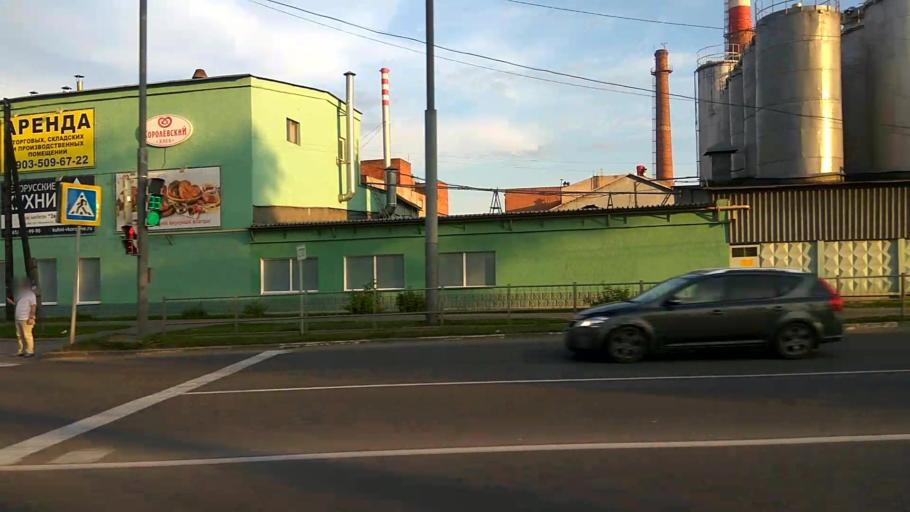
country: RU
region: Moskovskaya
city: Korolev
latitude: 55.9139
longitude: 37.8480
